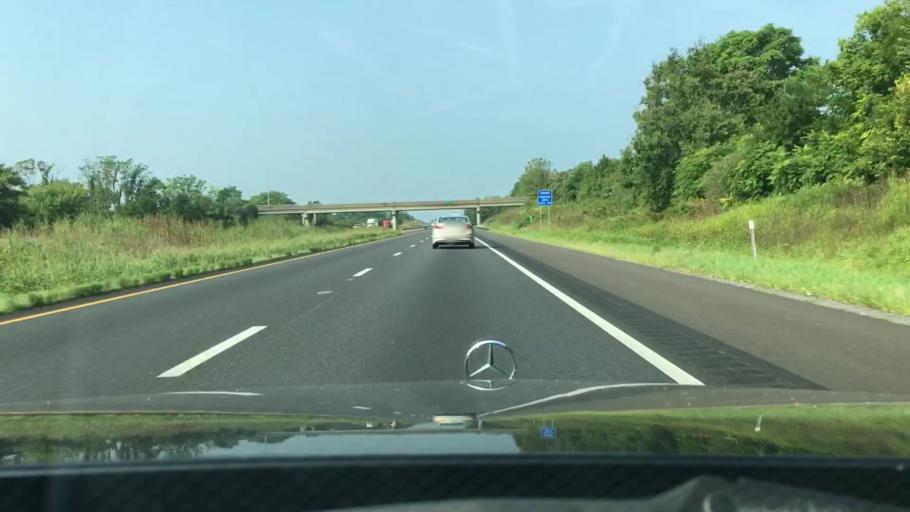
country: US
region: Virginia
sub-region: Shenandoah County
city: Strasburg
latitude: 39.0033
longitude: -78.3808
